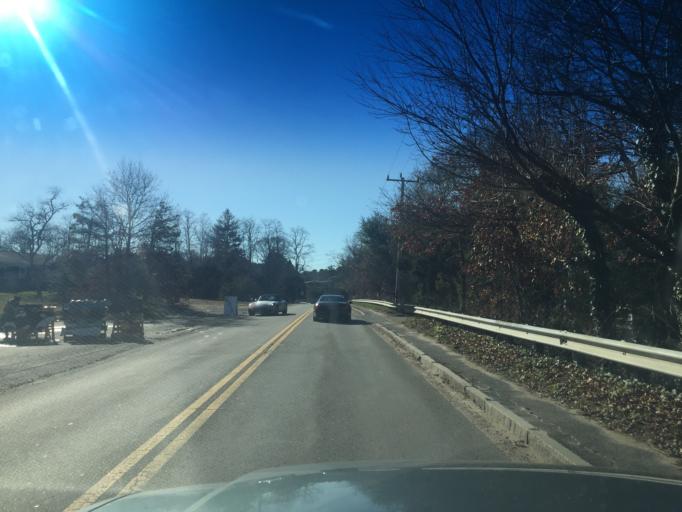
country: US
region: Massachusetts
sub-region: Barnstable County
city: North Falmouth
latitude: 41.6574
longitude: -70.6109
